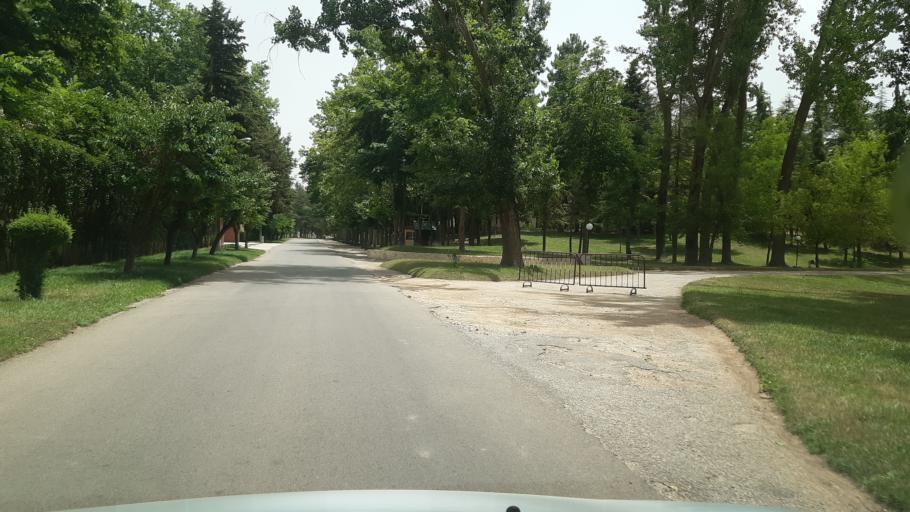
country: MA
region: Meknes-Tafilalet
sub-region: Ifrane
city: Ifrane
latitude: 33.6485
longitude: -5.0346
